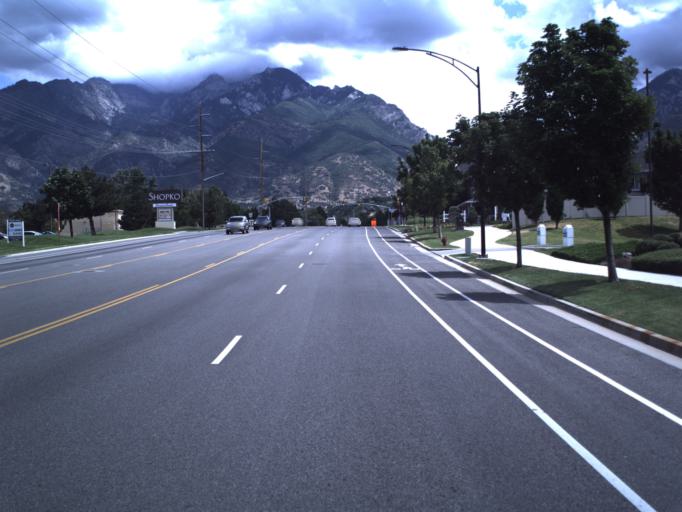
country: US
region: Utah
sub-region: Salt Lake County
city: Sandy Hills
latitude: 40.5804
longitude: -111.8314
